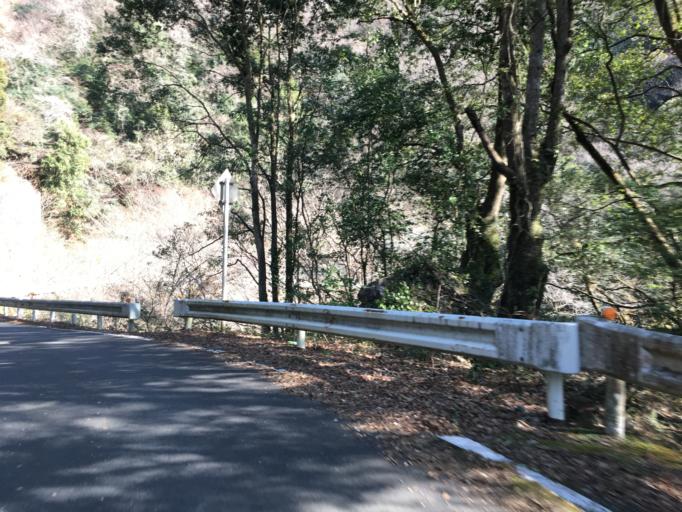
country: JP
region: Ibaraki
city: Kitaibaraki
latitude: 36.7825
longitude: 140.6771
